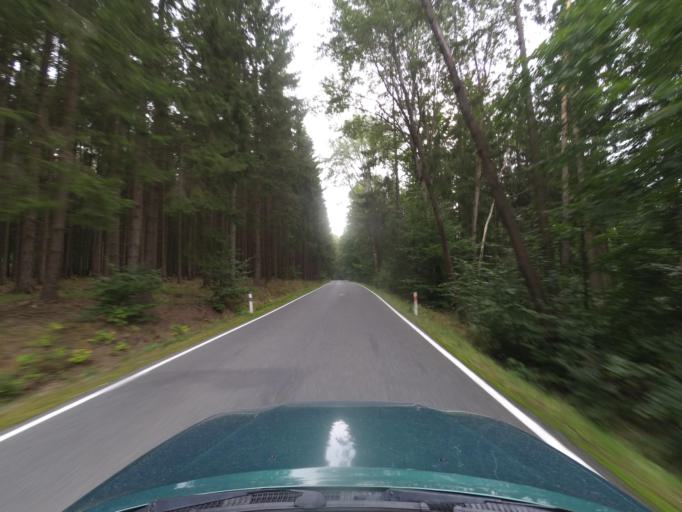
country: CZ
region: Plzensky
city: Bela nad Radbuzou
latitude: 49.5881
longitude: 12.6500
